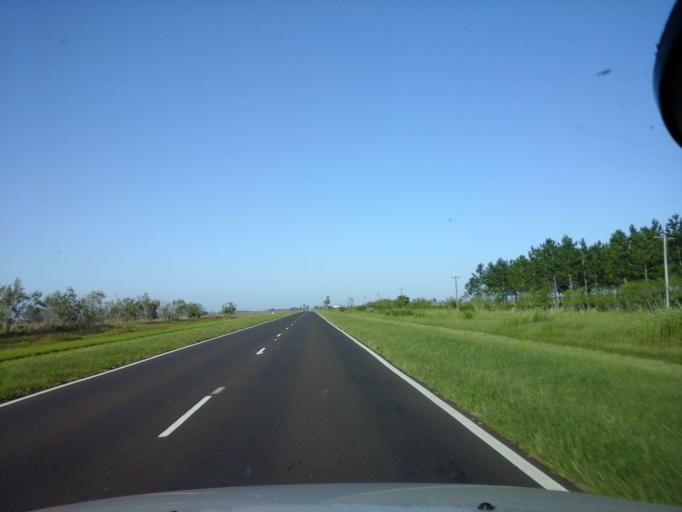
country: AR
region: Corrientes
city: Ita Ibate
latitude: -27.4496
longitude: -57.4055
